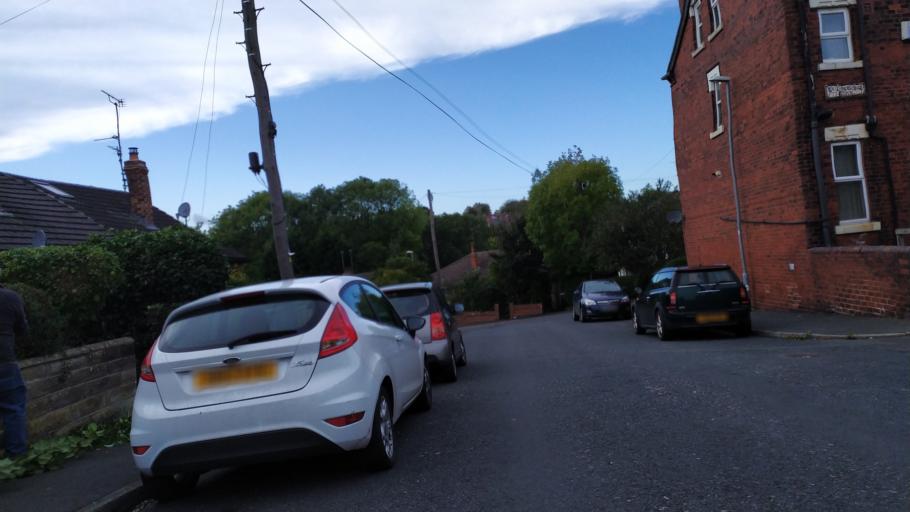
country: GB
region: England
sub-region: City and Borough of Leeds
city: Chapel Allerton
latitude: 53.8259
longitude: -1.5673
